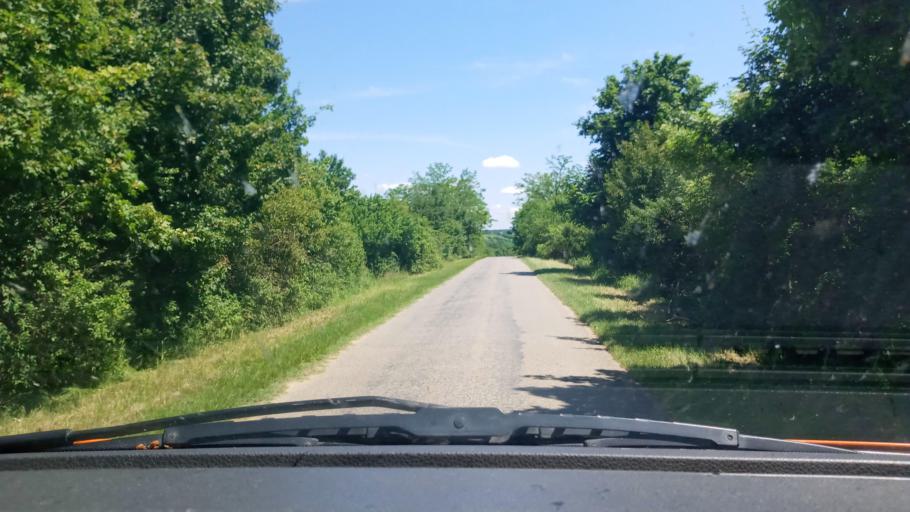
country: HU
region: Somogy
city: Kadarkut
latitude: 46.1752
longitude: 17.7451
